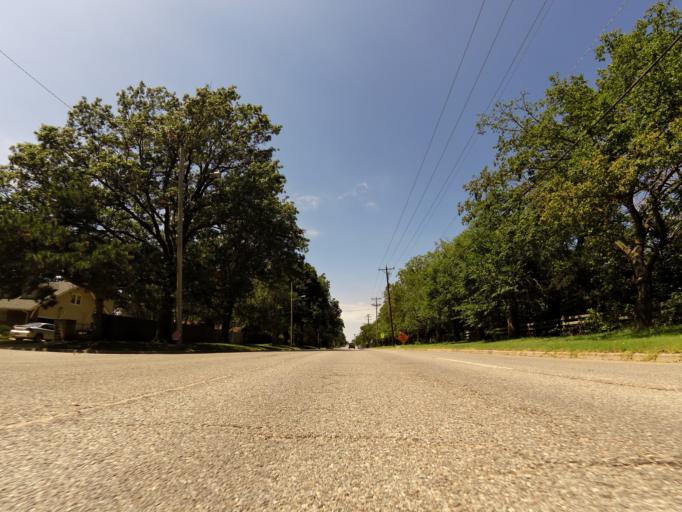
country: US
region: Kansas
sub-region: Sedgwick County
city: Bellaire
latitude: 37.7084
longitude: -97.2663
